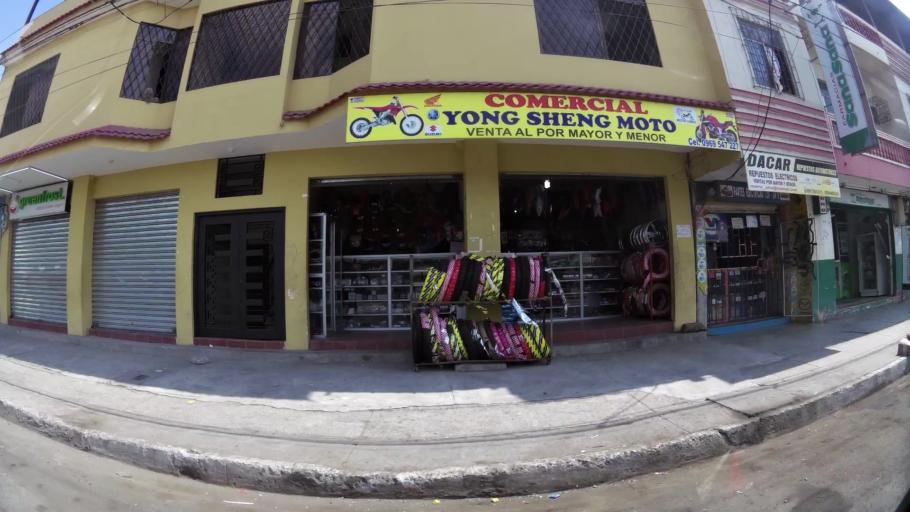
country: EC
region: Guayas
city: Eloy Alfaro
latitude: -2.1608
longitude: -79.8413
